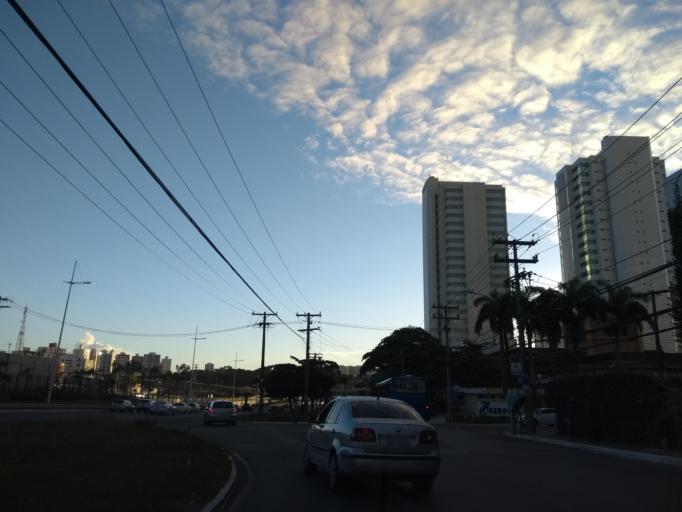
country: BR
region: Bahia
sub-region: Salvador
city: Salvador
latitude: -12.9648
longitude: -38.4372
